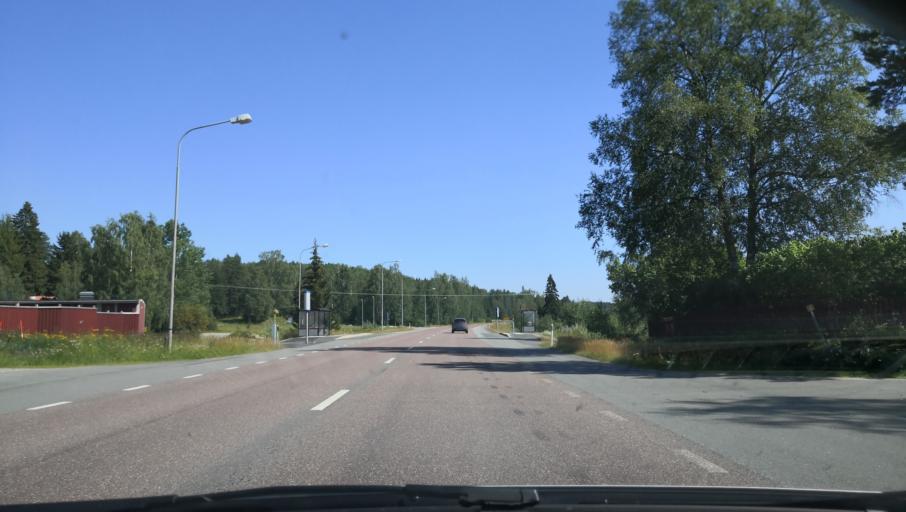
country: SE
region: Gaevleborg
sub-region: Ovanakers Kommun
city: Alfta
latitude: 61.3346
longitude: 16.2176
